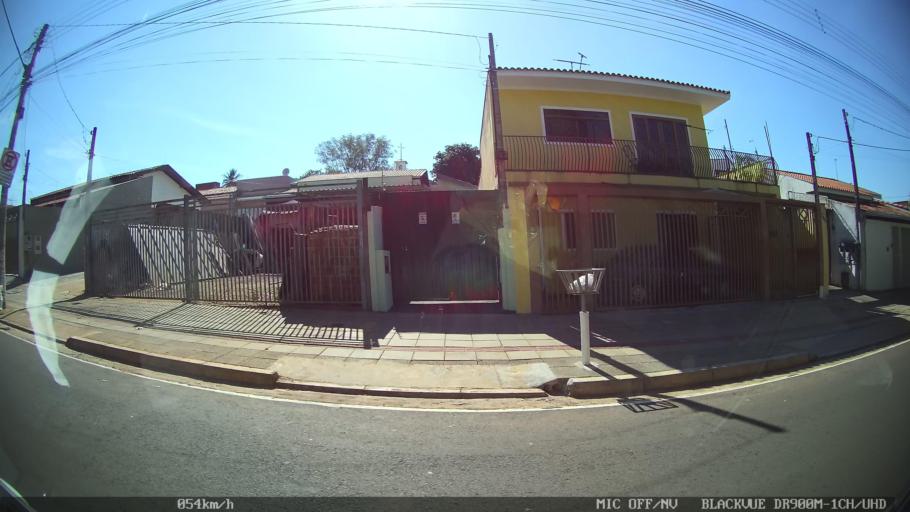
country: BR
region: Sao Paulo
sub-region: Sao Jose Do Rio Preto
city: Sao Jose do Rio Preto
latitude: -20.7773
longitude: -49.3892
